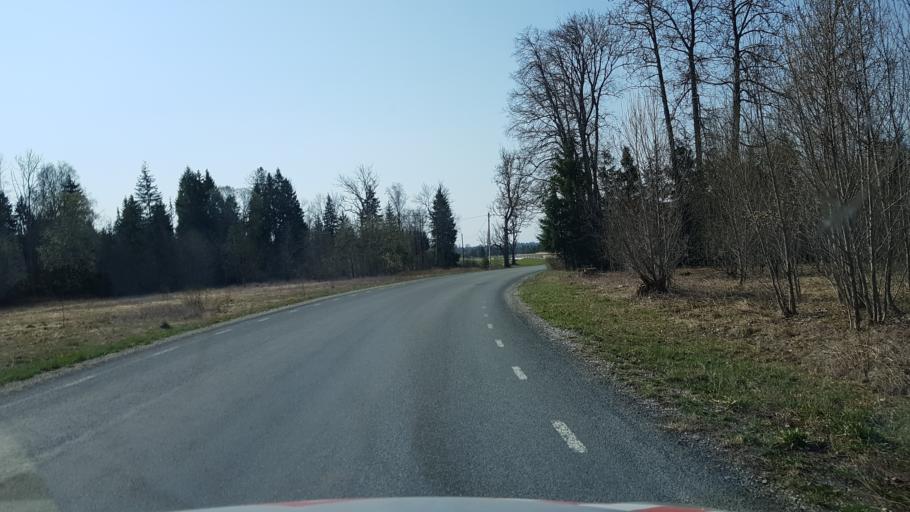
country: EE
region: Raplamaa
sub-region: Maerjamaa vald
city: Marjamaa
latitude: 58.8705
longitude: 24.3739
